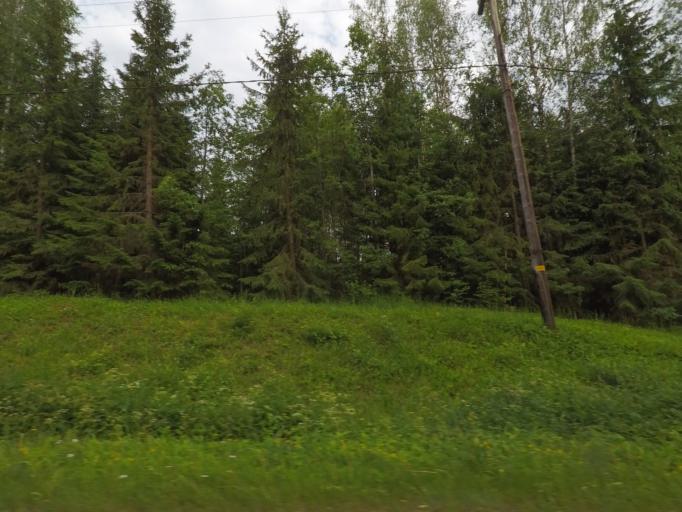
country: FI
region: Paijanne Tavastia
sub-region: Lahti
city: Hollola
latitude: 60.8888
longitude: 25.5136
